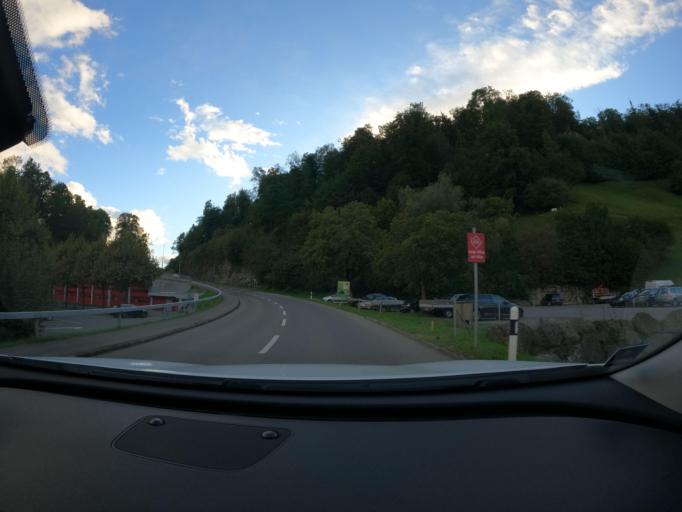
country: CH
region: Obwalden
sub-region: Obwalden
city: Sarnen
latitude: 46.8988
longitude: 8.2441
